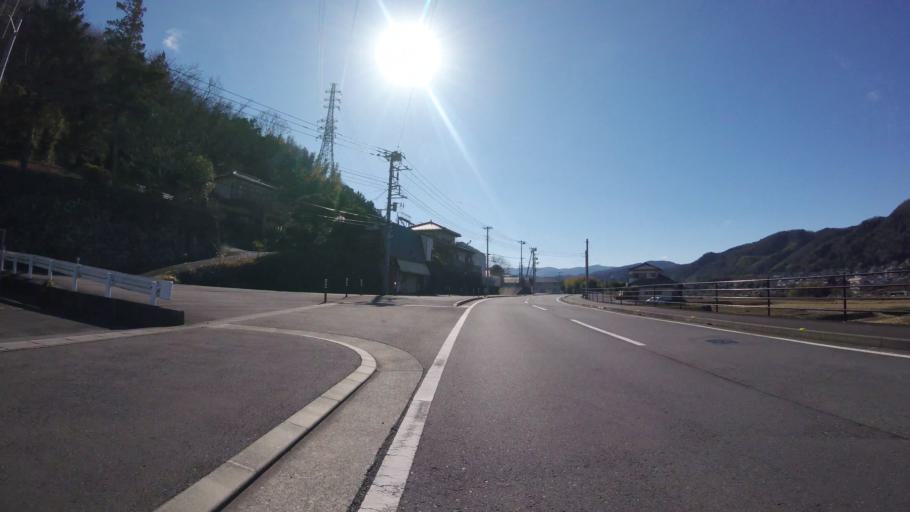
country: JP
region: Shizuoka
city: Ito
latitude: 34.9700
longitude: 138.9492
